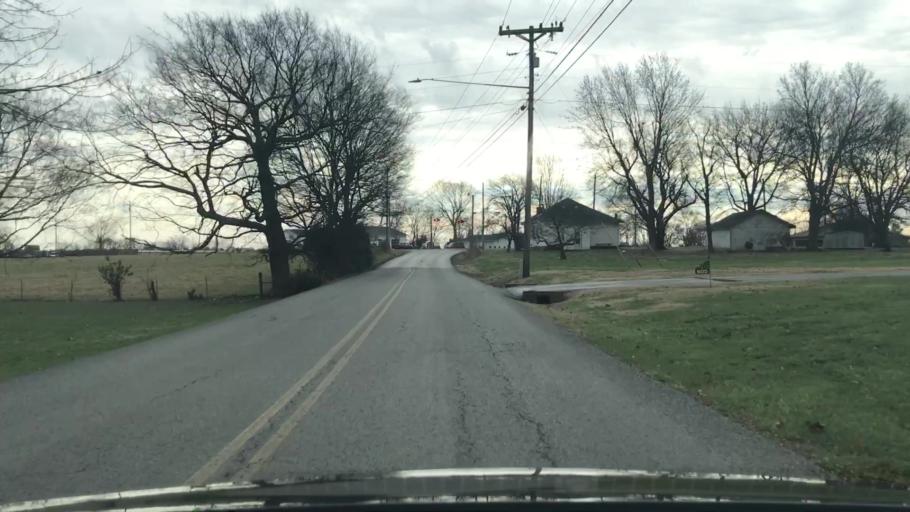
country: US
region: Kentucky
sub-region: Christian County
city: Hopkinsville
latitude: 36.8635
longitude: -87.5382
